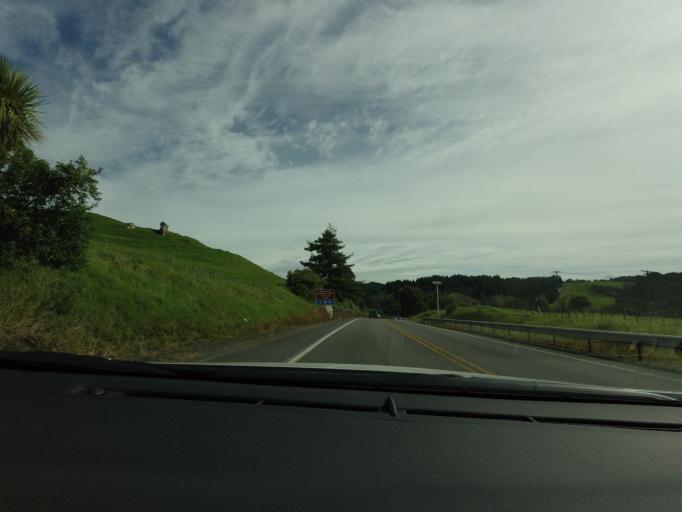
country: NZ
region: Auckland
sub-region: Auckland
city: Warkworth
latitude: -36.4880
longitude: 174.6608
